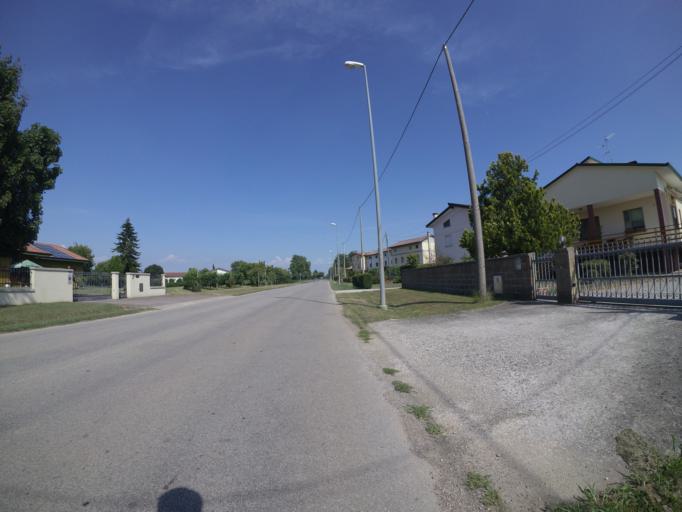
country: IT
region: Friuli Venezia Giulia
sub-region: Provincia di Udine
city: Lestizza
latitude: 45.9562
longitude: 13.1491
